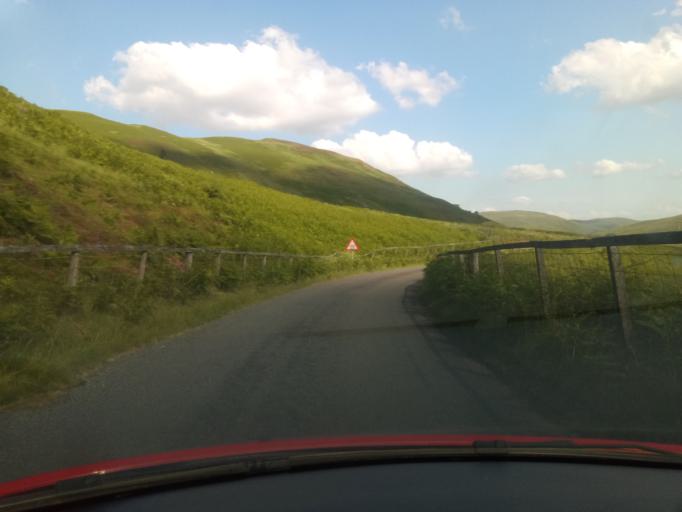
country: GB
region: Scotland
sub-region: The Scottish Borders
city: Innerleithen
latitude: 55.4659
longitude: -3.1288
